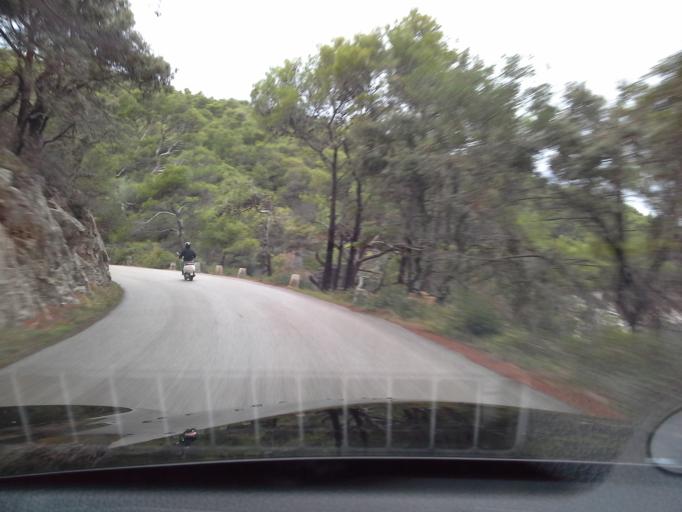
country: HR
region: Primorsko-Goranska
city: Mali Losinj
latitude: 44.5233
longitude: 14.4909
